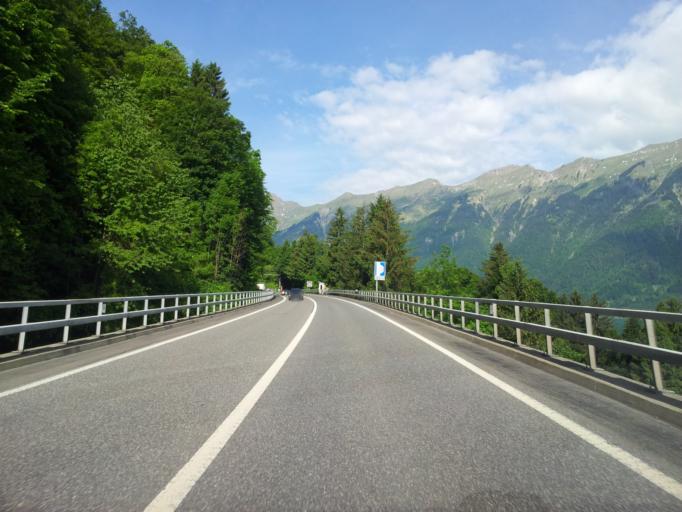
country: CH
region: Bern
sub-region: Interlaken-Oberhasli District
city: Brienz
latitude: 46.7394
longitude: 8.0398
